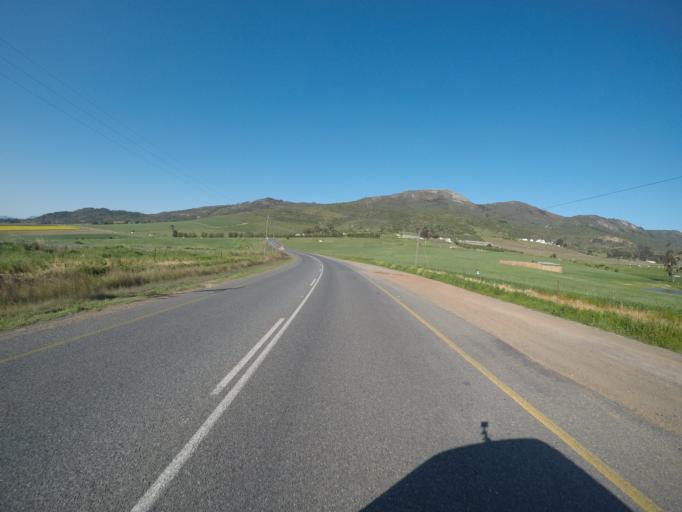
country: ZA
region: Western Cape
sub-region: Cape Winelands District Municipality
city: Noorder-Paarl
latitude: -33.7081
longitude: 18.8884
